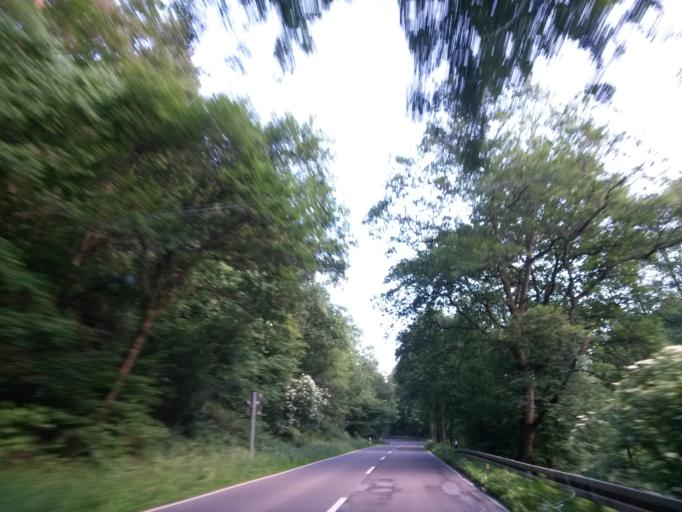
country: DE
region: North Rhine-Westphalia
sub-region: Regierungsbezirk Koln
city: Overath
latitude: 50.9159
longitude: 7.3272
